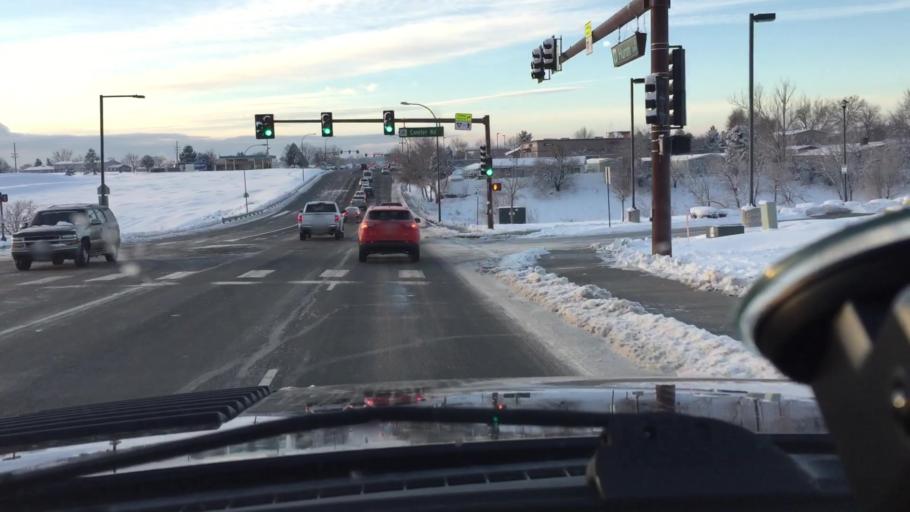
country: US
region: Colorado
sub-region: Adams County
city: Federal Heights
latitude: 39.8668
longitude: -104.9967
